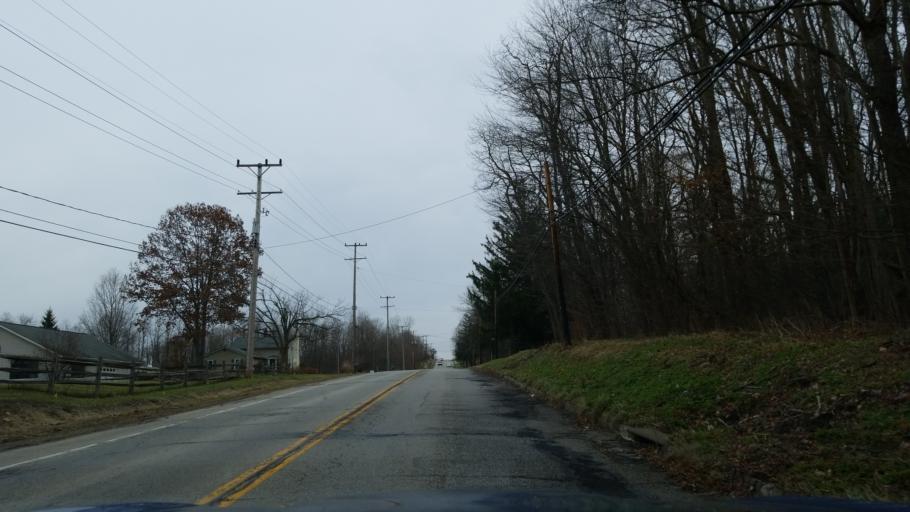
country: US
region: Ohio
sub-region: Geauga County
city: Bainbridge
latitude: 41.3873
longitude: -81.2555
